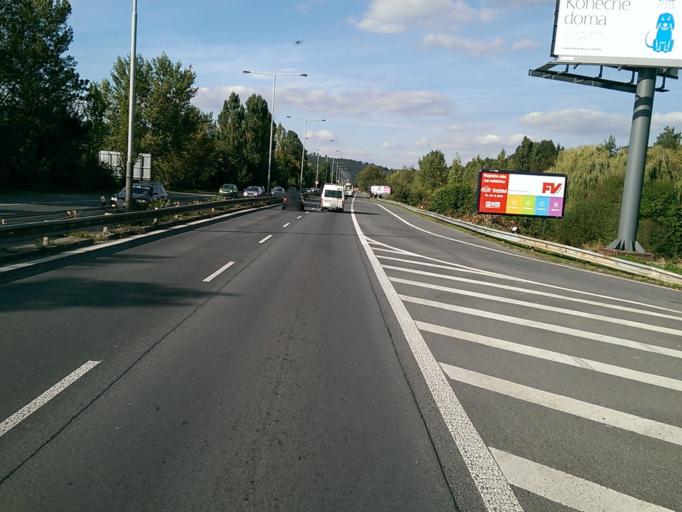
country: CZ
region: Praha
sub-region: Praha 12
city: Modrany
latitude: 50.0034
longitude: 14.3952
